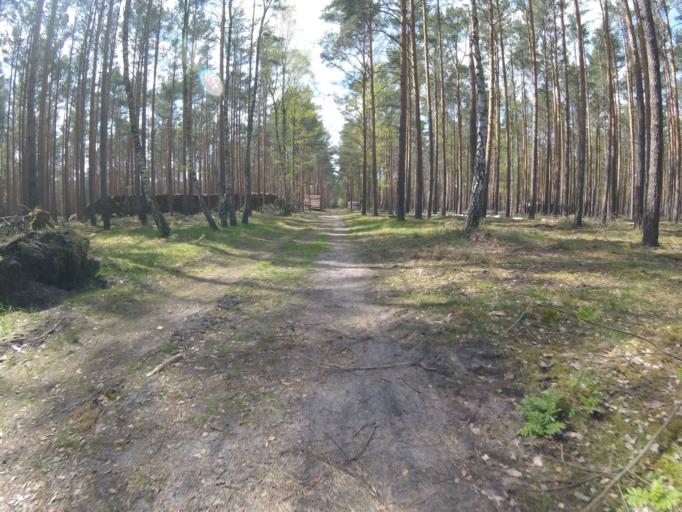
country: DE
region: Brandenburg
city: Gross Koris
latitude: 52.1982
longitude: 13.7015
